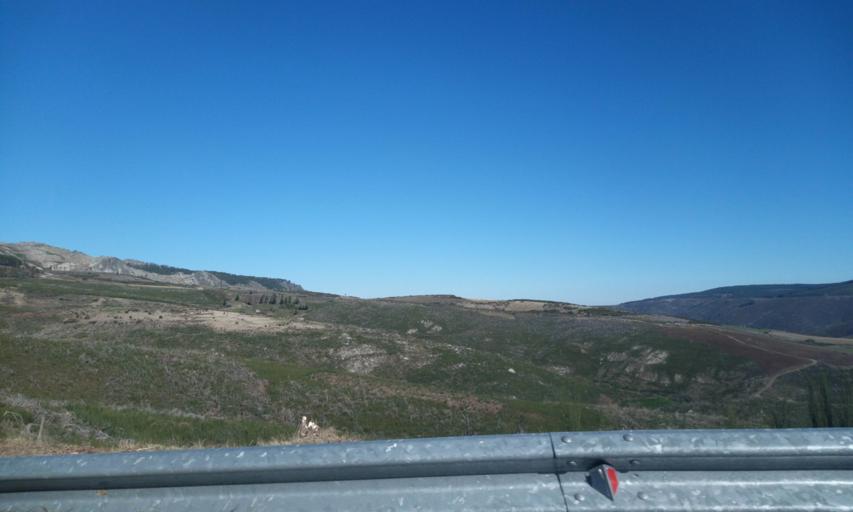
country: PT
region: Guarda
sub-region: Manteigas
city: Manteigas
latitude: 40.4626
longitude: -7.5131
